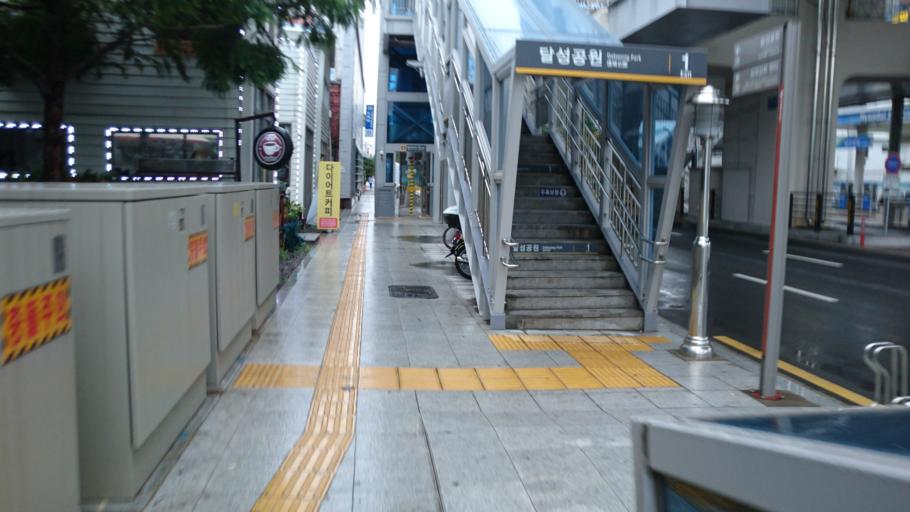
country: KR
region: Daegu
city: Daegu
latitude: 35.8759
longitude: 128.5822
